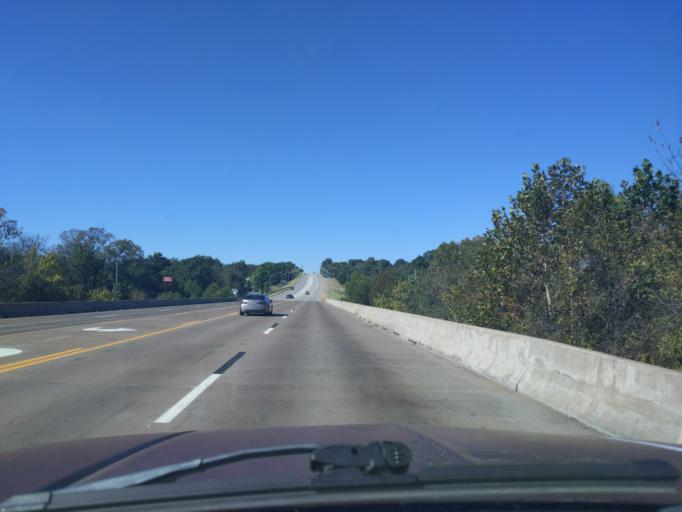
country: US
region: Oklahoma
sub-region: Creek County
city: Sapulpa
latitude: 35.9884
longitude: -96.0814
